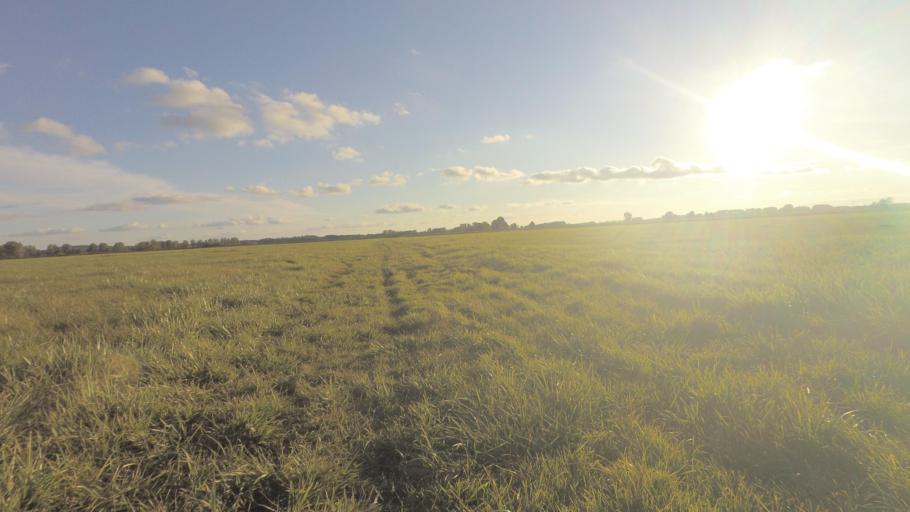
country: DE
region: Brandenburg
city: Rangsdorf
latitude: 52.3025
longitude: 13.3573
